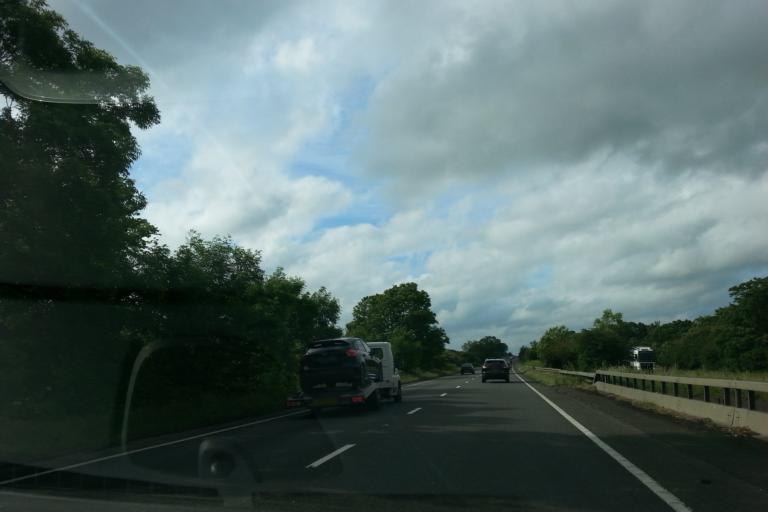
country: GB
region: England
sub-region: District of Rutland
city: Clipsham
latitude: 52.7139
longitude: -0.5930
